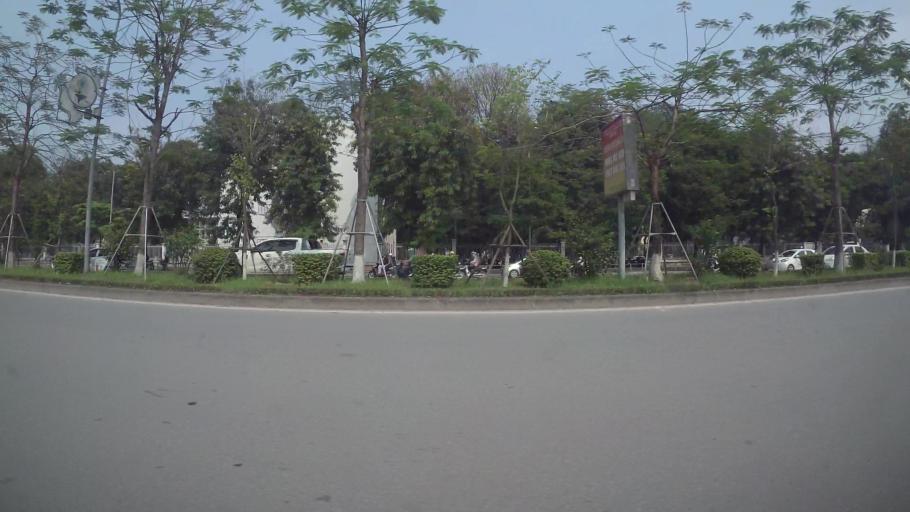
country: VN
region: Ha Noi
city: Hai BaTrung
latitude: 21.0055
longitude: 105.8413
